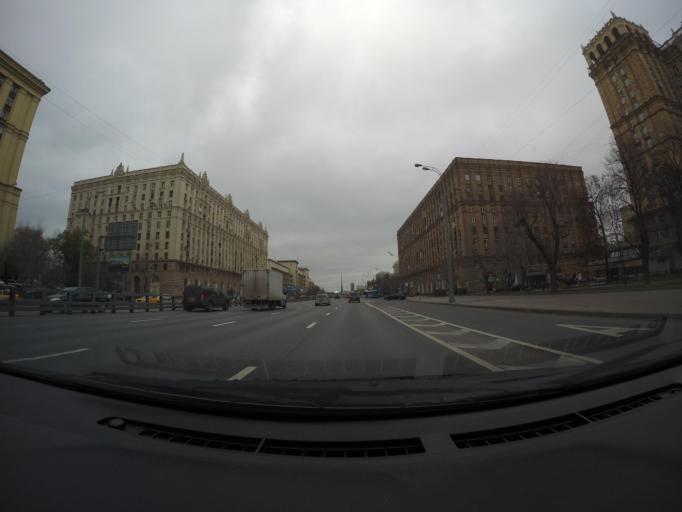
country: RU
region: Moscow
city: Mar'ina Roshcha
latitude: 55.8128
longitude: 37.6376
